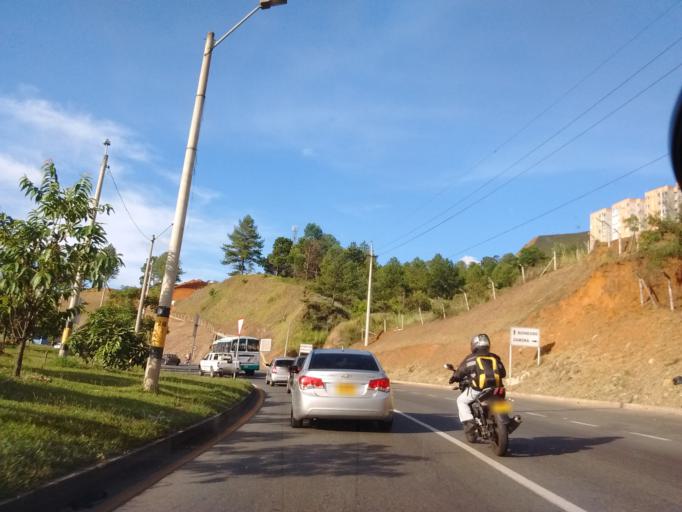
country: CO
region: Antioquia
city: Bello
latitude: 6.3112
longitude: -75.5503
